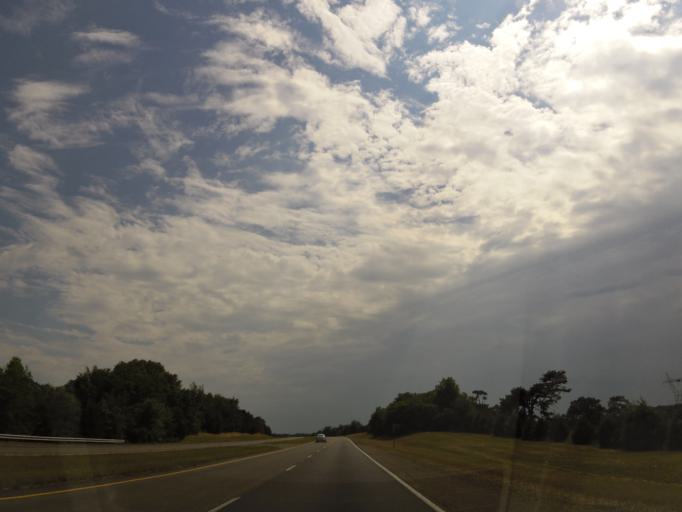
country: US
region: Alabama
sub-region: Jackson County
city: Stevenson
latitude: 34.7632
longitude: -85.9033
